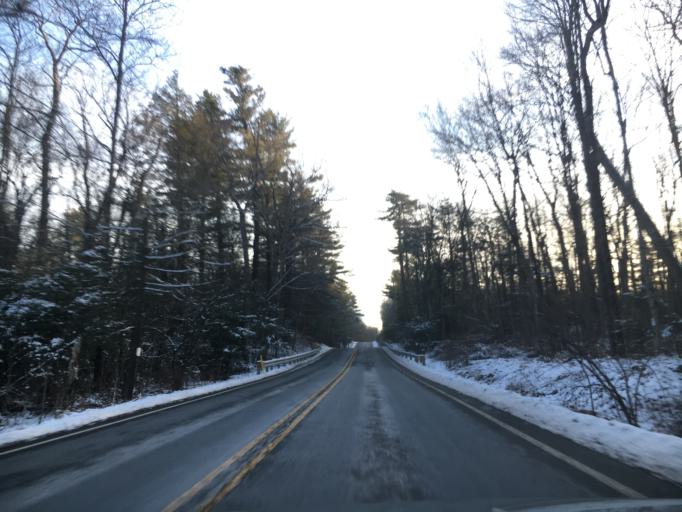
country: US
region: Pennsylvania
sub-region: Pike County
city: Hemlock Farms
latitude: 41.3630
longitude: -75.1280
